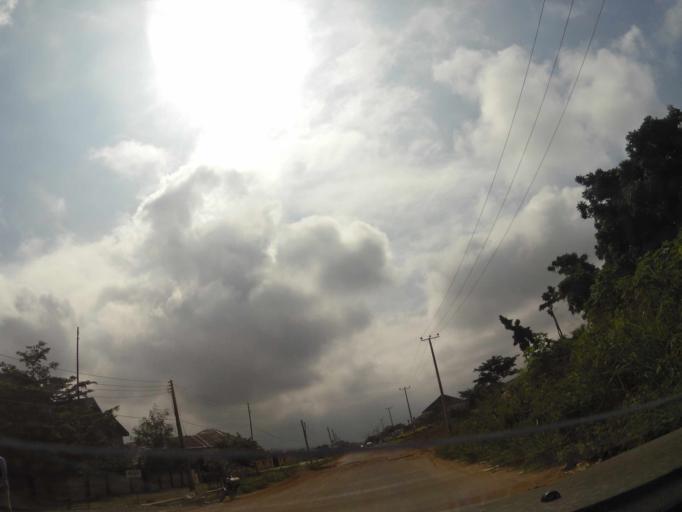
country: NG
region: Oyo
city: Ibadan
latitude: 7.4393
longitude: 3.9597
